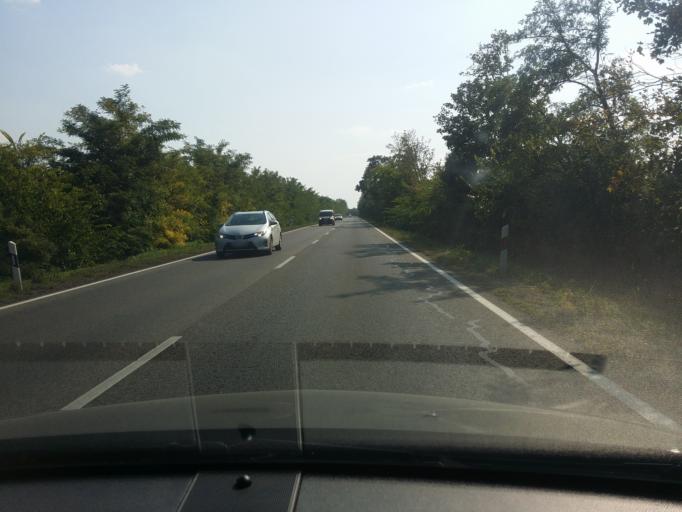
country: HU
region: Fejer
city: dunaujvaros
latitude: 46.9529
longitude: 18.9119
